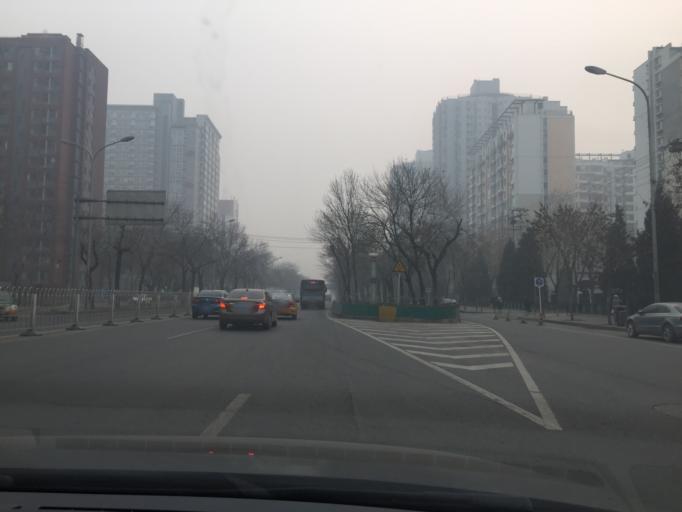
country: CN
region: Beijing
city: Qinghe
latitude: 40.0130
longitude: 116.3459
